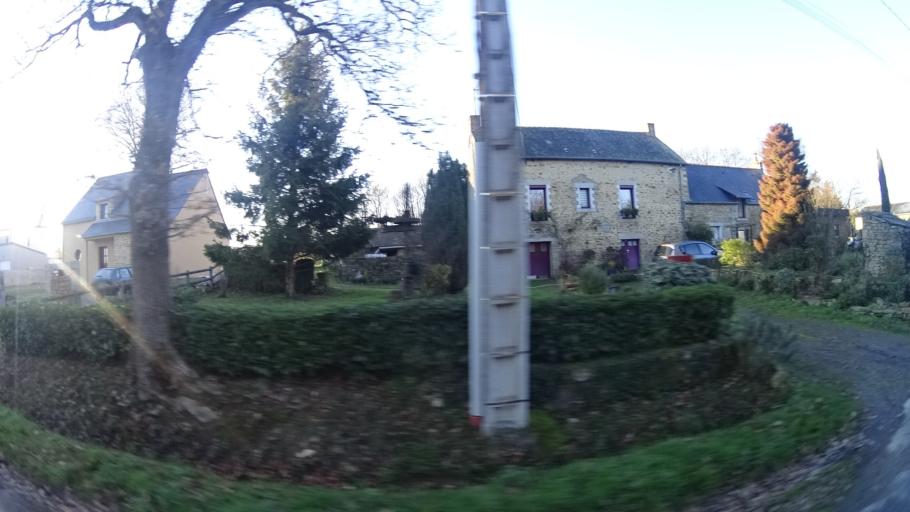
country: FR
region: Brittany
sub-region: Departement du Morbihan
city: Saint-Perreux
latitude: 47.6580
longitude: -2.1194
